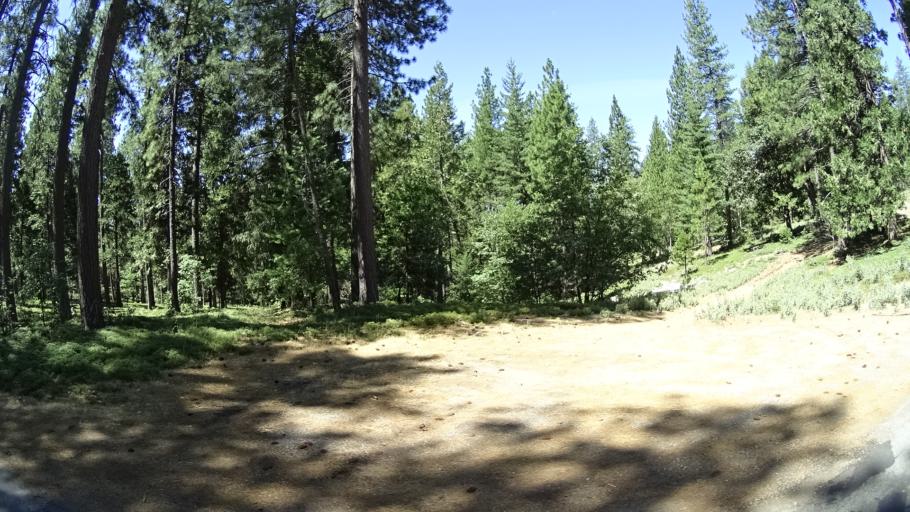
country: US
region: California
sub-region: Amador County
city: Pioneer
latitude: 38.4199
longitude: -120.4951
